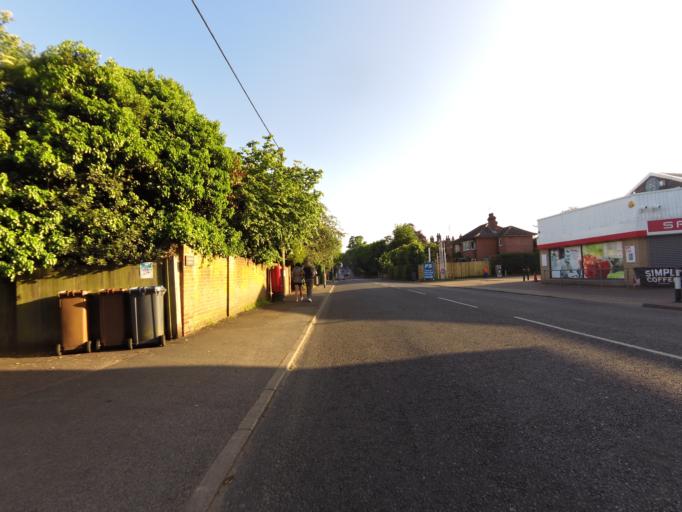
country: GB
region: England
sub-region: Suffolk
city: Woodbridge
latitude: 52.1003
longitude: 1.3257
